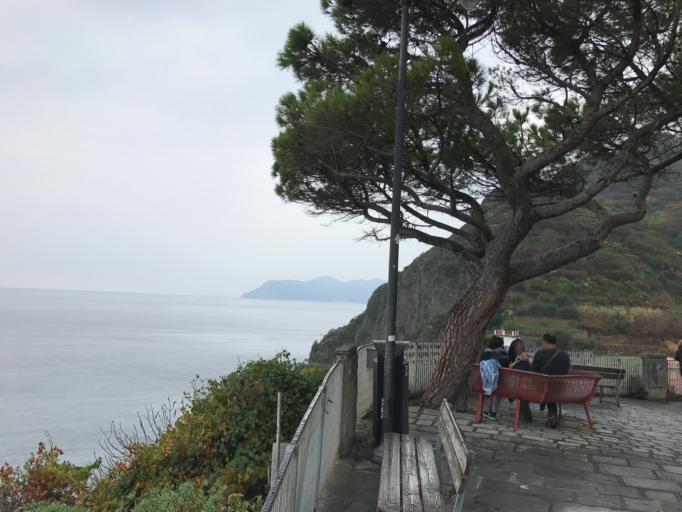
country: IT
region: Liguria
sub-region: Provincia di La Spezia
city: Riomaggiore
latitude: 44.0995
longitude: 9.7367
